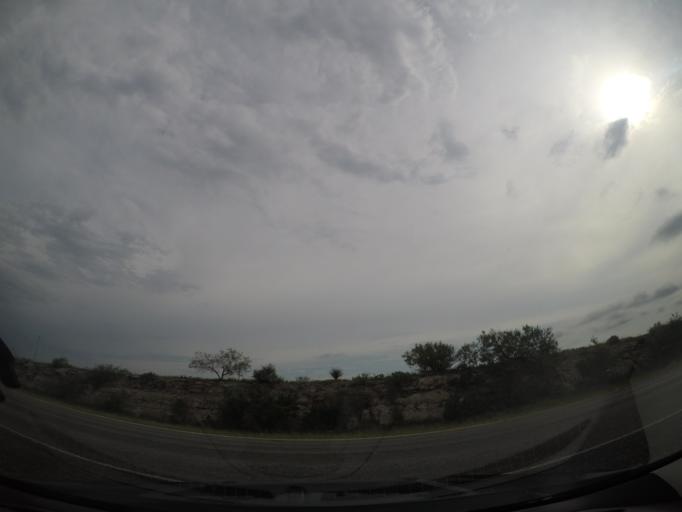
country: US
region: Texas
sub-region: Val Verde County
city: Cienegas Terrace
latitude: 29.8175
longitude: -101.5502
